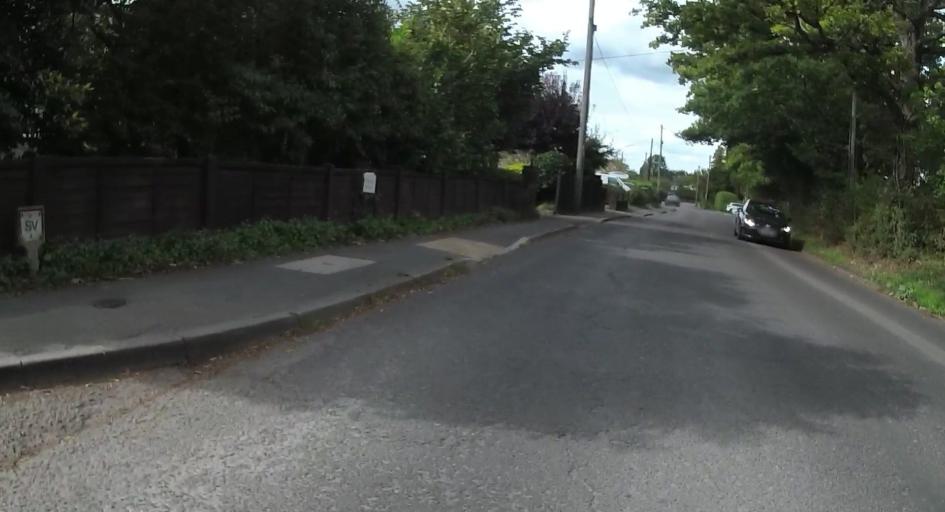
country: GB
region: England
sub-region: Surrey
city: Knaphill
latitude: 51.3373
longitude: -0.6341
